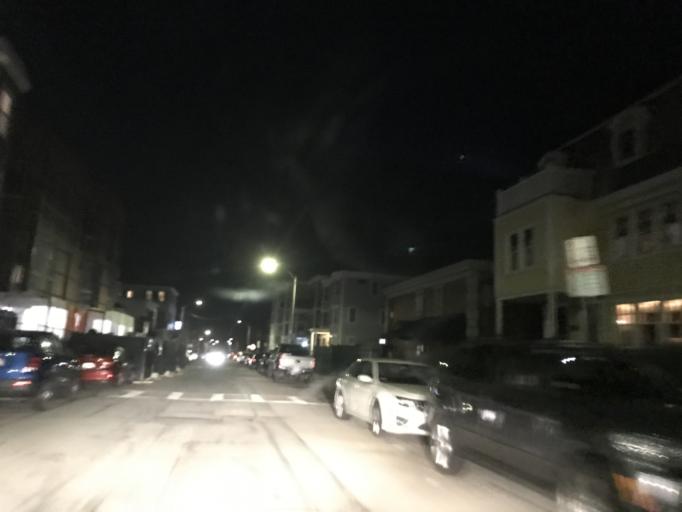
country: US
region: Massachusetts
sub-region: Suffolk County
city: South Boston
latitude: 42.3333
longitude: -71.0284
